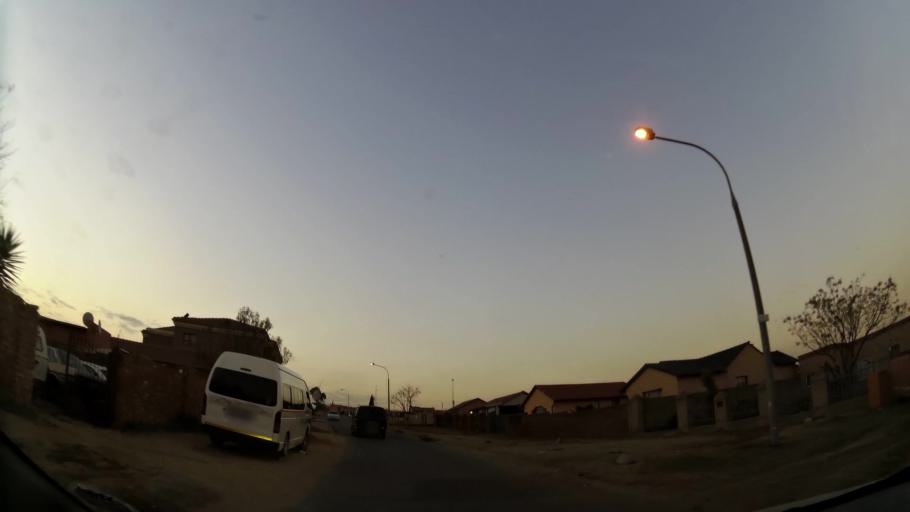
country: ZA
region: Gauteng
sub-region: West Rand District Municipality
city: Randfontein
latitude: -26.2101
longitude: 27.7138
